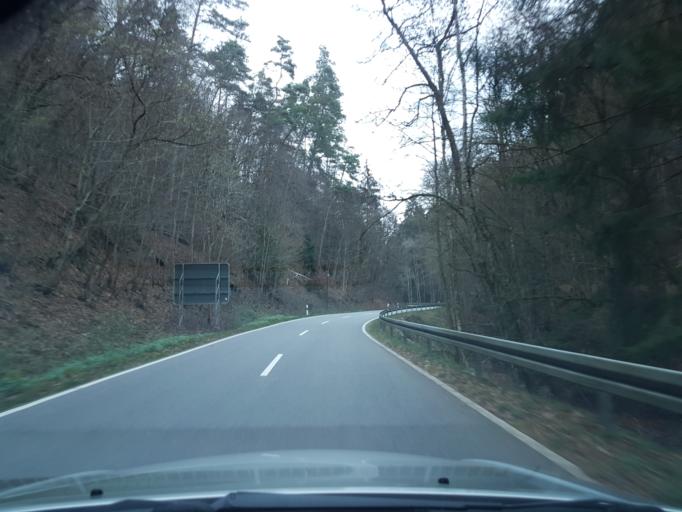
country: DE
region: Hesse
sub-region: Regierungsbezirk Darmstadt
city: Bad Schwalbach
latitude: 50.1200
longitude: 7.9803
